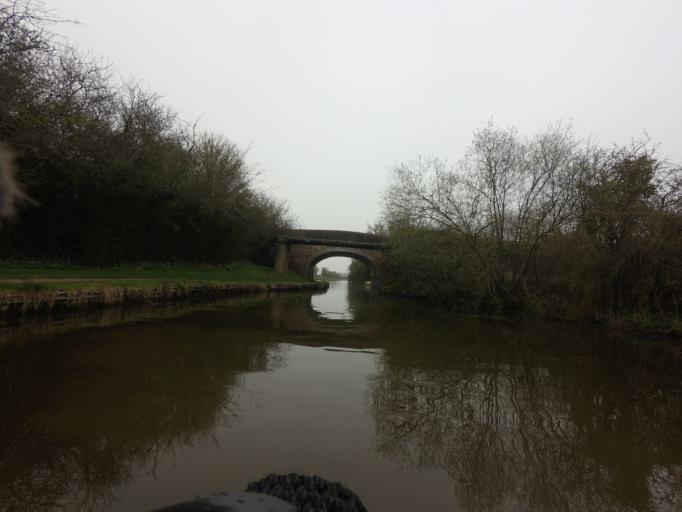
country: GB
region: England
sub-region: Hertfordshire
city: Tring
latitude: 51.7900
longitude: -0.6182
